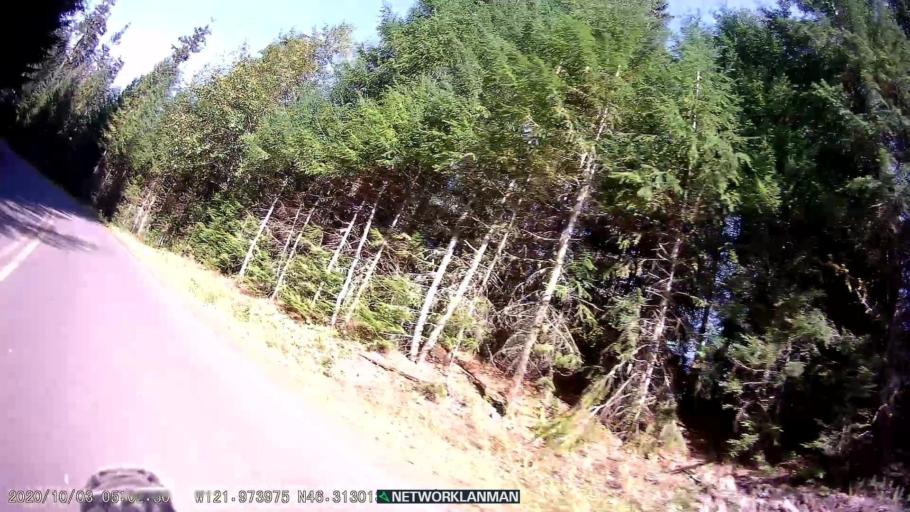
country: US
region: Washington
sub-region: Lewis County
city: Morton
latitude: 46.3132
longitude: -121.9743
